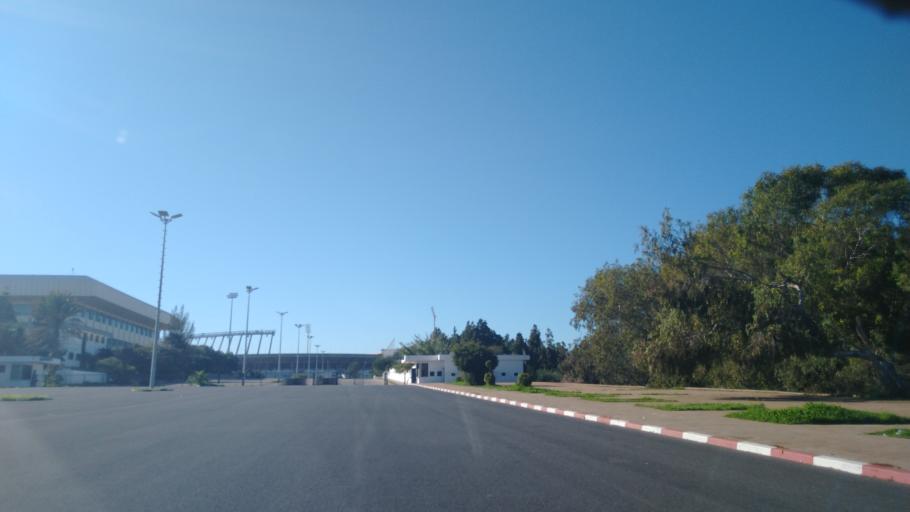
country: MA
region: Rabat-Sale-Zemmour-Zaer
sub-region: Skhirate-Temara
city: Temara
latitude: 33.9649
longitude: -6.8872
